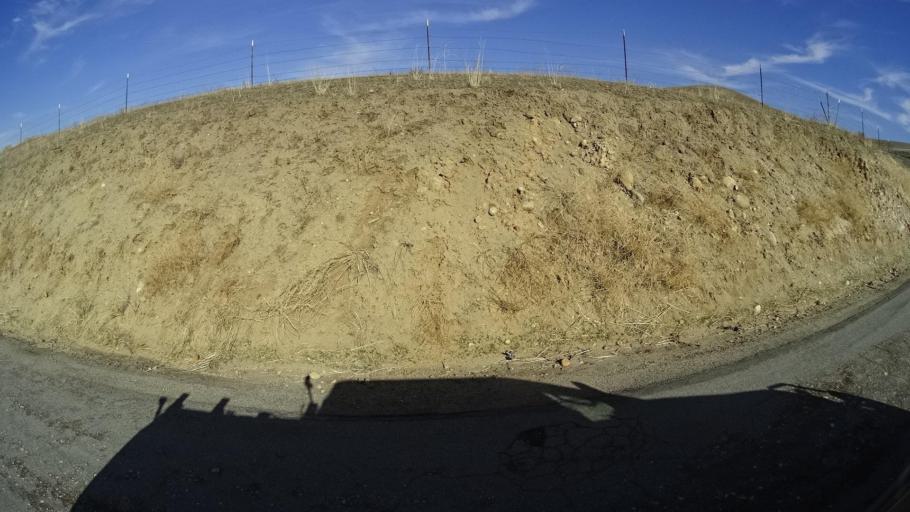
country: US
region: California
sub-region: Kern County
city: Lamont
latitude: 35.3991
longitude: -118.7780
